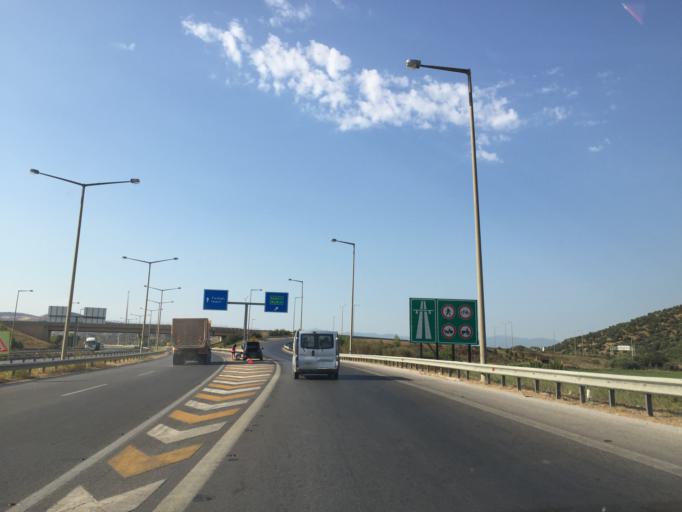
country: TR
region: Izmir
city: Belevi
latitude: 38.0293
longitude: 27.4441
